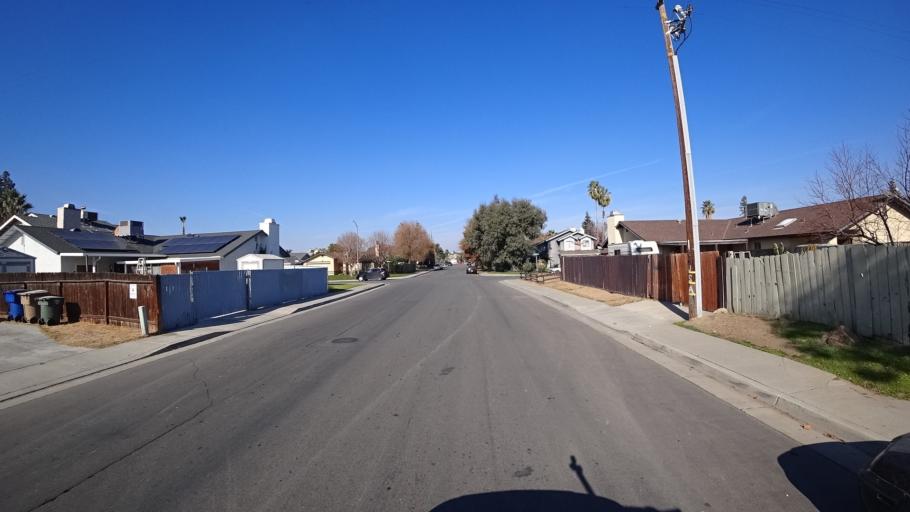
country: US
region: California
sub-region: Kern County
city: Greenfield
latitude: 35.2995
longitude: -119.0421
